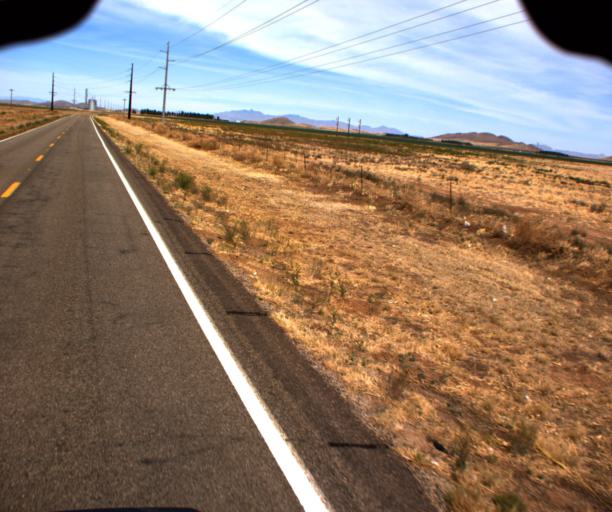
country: US
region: Arizona
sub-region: Cochise County
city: Tombstone
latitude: 31.8153
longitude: -109.6948
